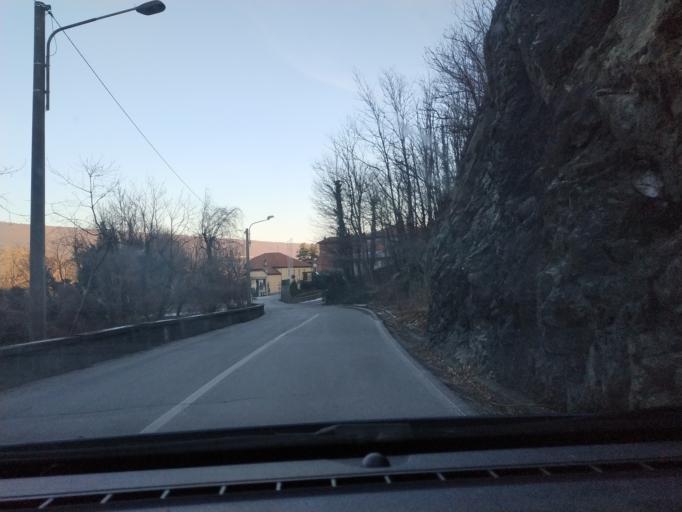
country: IT
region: Piedmont
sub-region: Provincia di Torino
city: Ivrea
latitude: 45.4824
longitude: 7.8765
